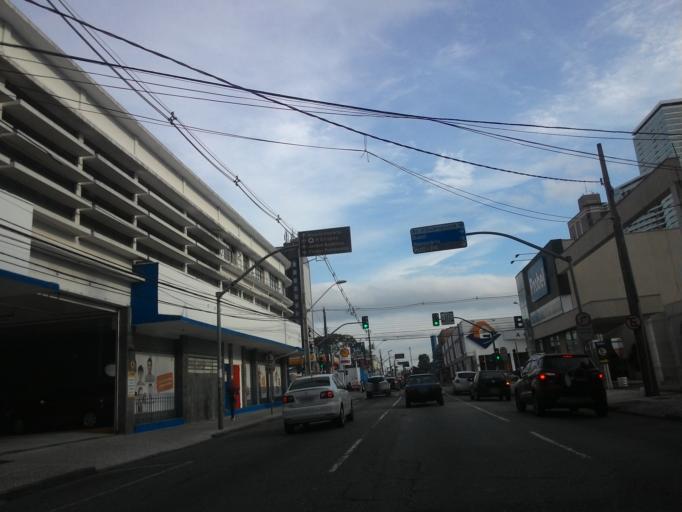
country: BR
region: Parana
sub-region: Curitiba
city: Curitiba
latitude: -25.4336
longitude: -49.2621
